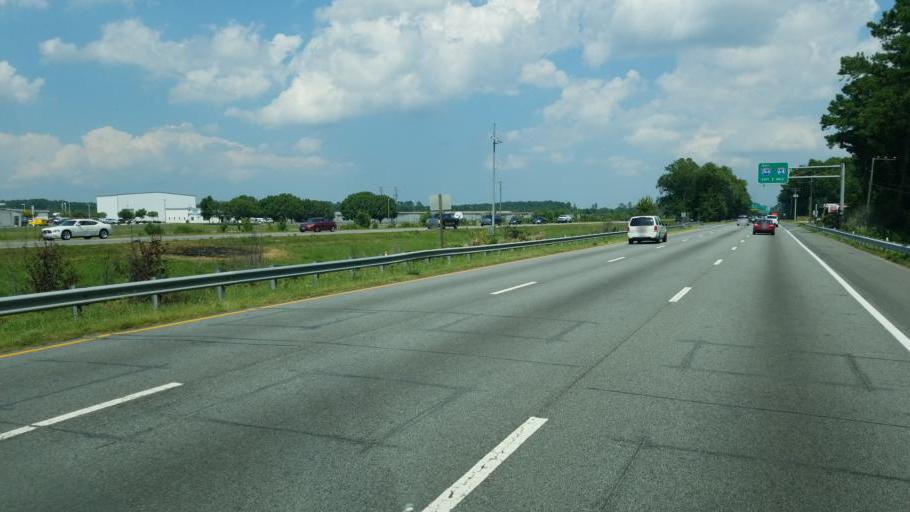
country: US
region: Virginia
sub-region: City of Portsmouth
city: Portsmouth Heights
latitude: 36.7752
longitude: -76.4481
